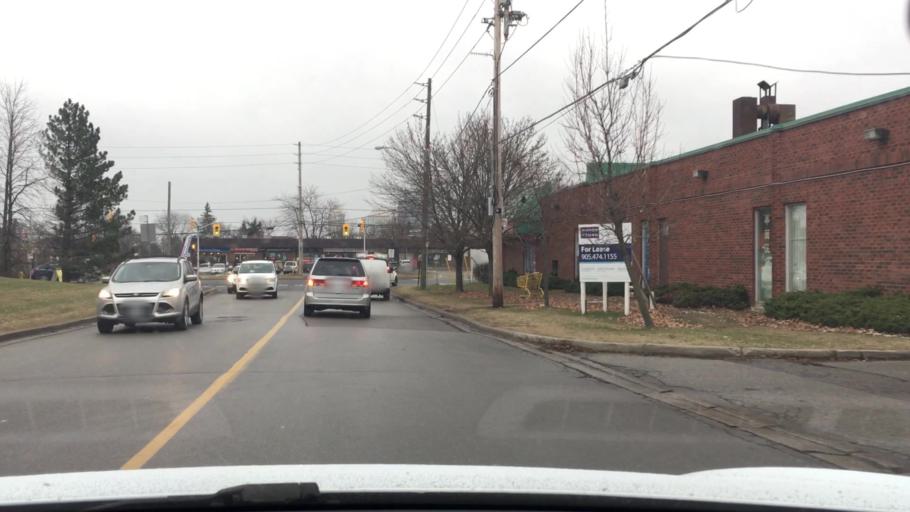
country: CA
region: Ontario
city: Scarborough
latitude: 43.7925
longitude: -79.2493
